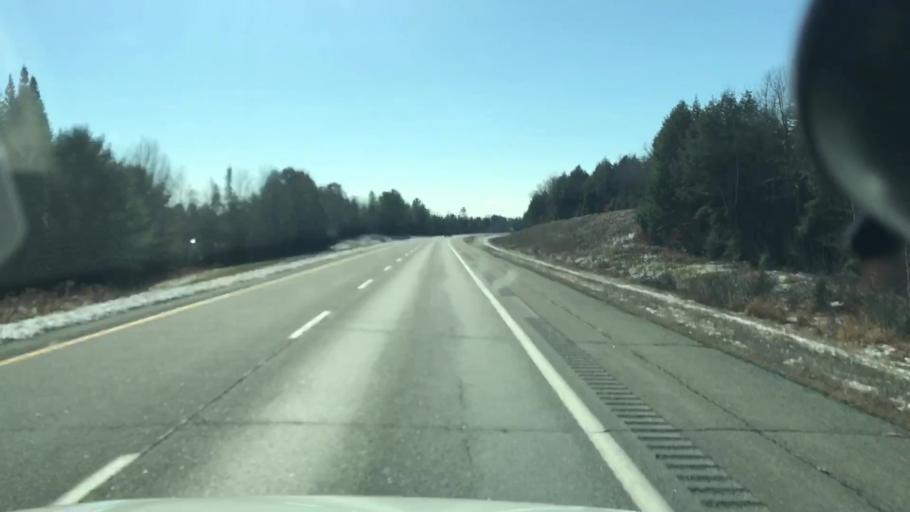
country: US
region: Maine
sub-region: Penobscot County
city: Howland
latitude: 45.2924
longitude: -68.6652
